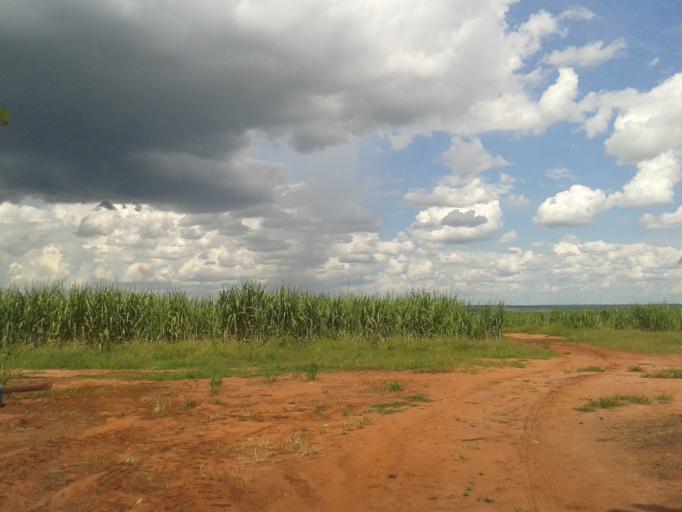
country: BR
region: Minas Gerais
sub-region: Santa Vitoria
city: Santa Vitoria
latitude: -19.1607
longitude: -50.6002
